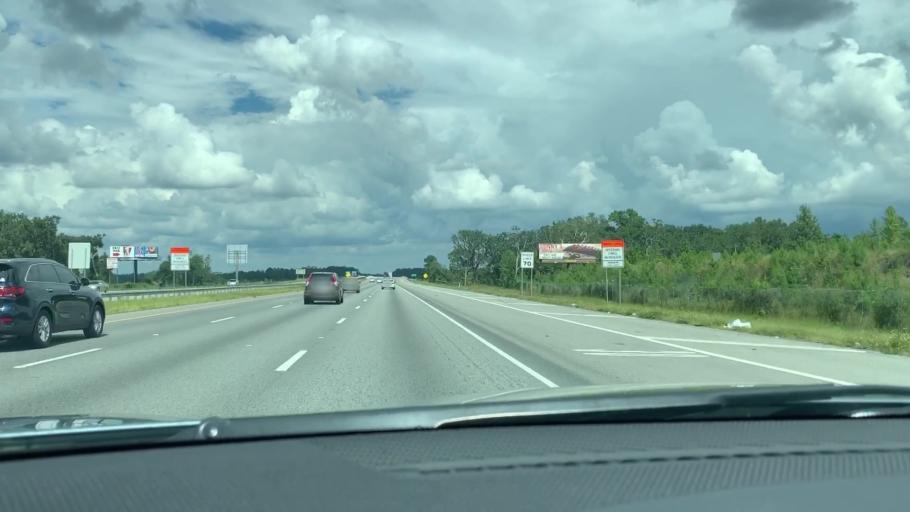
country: US
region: Georgia
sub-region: Glynn County
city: Dock Junction
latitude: 31.1471
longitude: -81.5684
